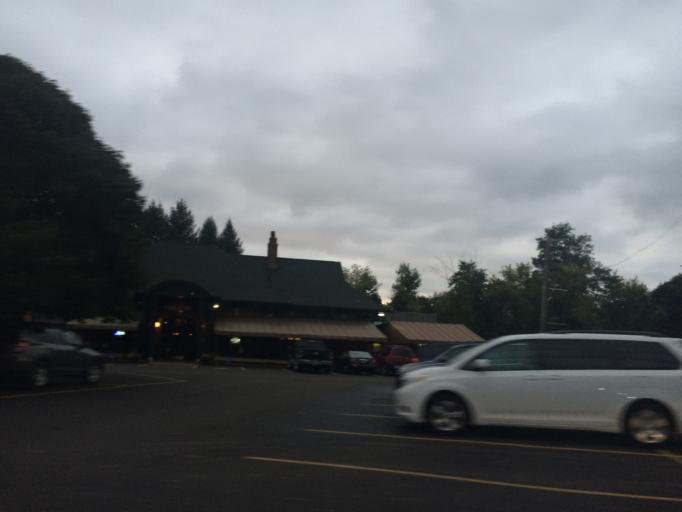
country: US
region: New York
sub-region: Erie County
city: East Aurora
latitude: 42.7688
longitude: -78.6115
